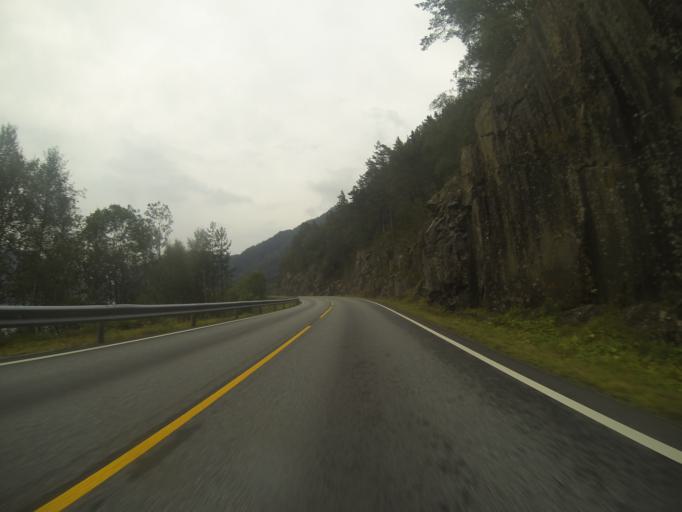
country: NO
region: Rogaland
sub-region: Suldal
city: Sand
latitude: 59.4718
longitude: 6.1855
